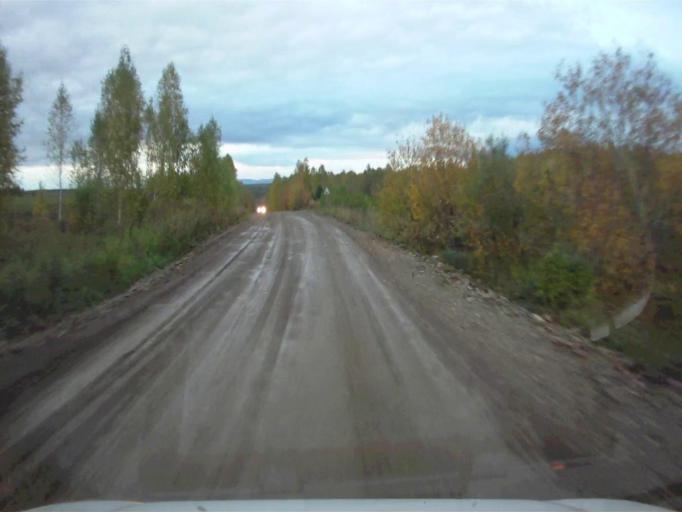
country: RU
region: Sverdlovsk
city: Mikhaylovsk
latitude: 56.2088
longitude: 59.2093
